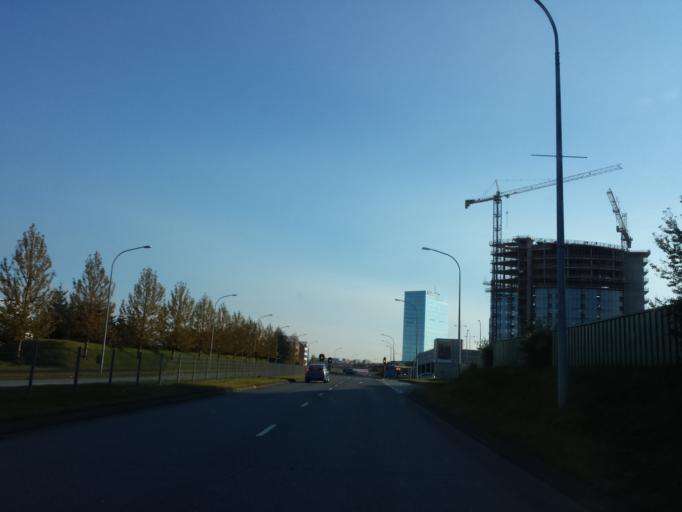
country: IS
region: Capital Region
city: Kopavogur
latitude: 64.1022
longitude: -21.8907
